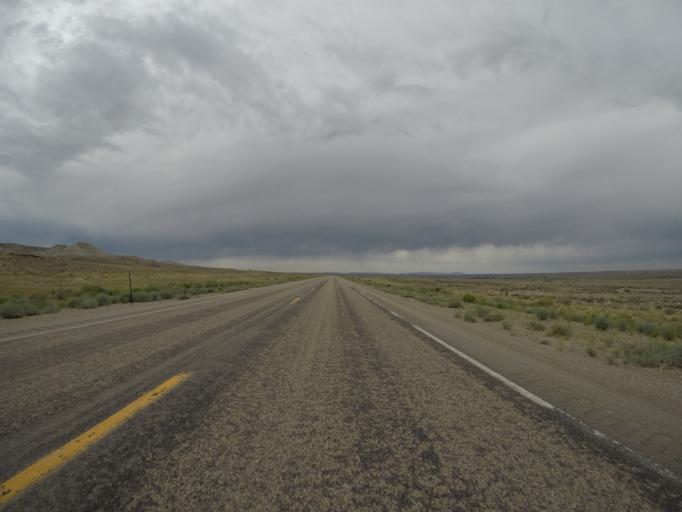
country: US
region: Wyoming
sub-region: Lincoln County
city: Kemmerer
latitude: 41.9461
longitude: -110.0092
